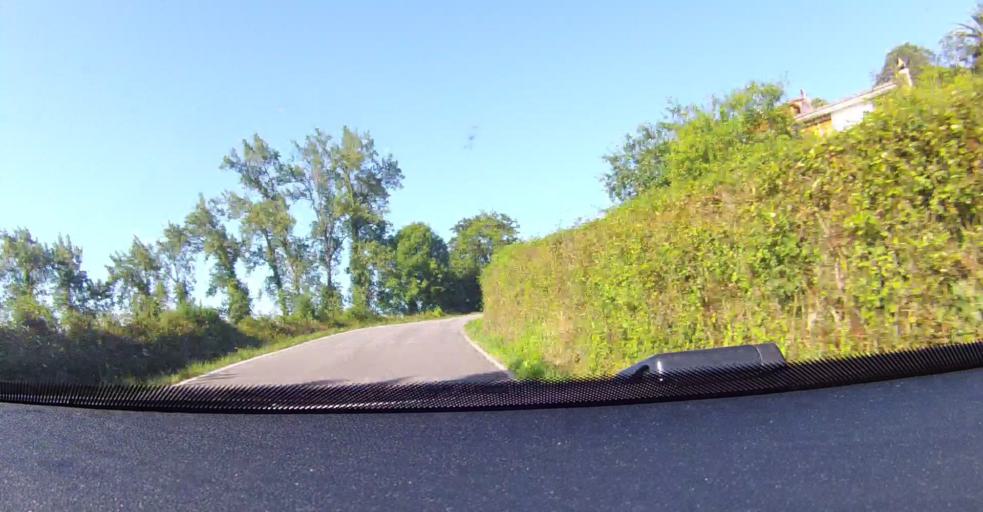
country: ES
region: Asturias
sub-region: Province of Asturias
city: Villaviciosa
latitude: 43.4802
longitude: -5.4308
